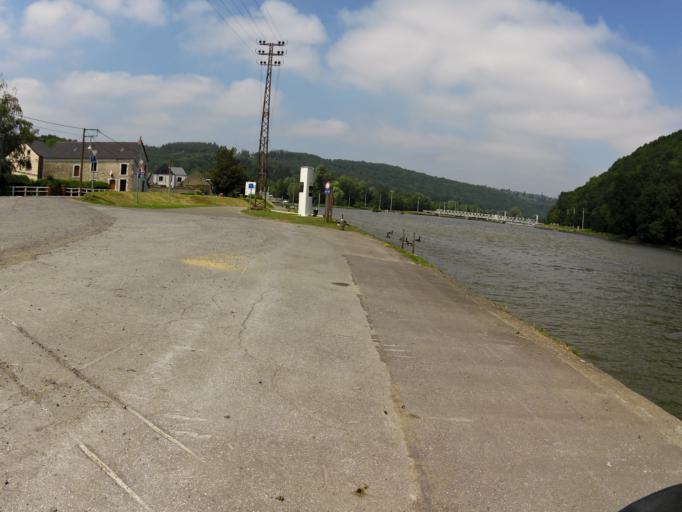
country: BE
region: Wallonia
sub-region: Province de Namur
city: Hastiere-Lavaux
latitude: 50.1966
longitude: 4.8211
